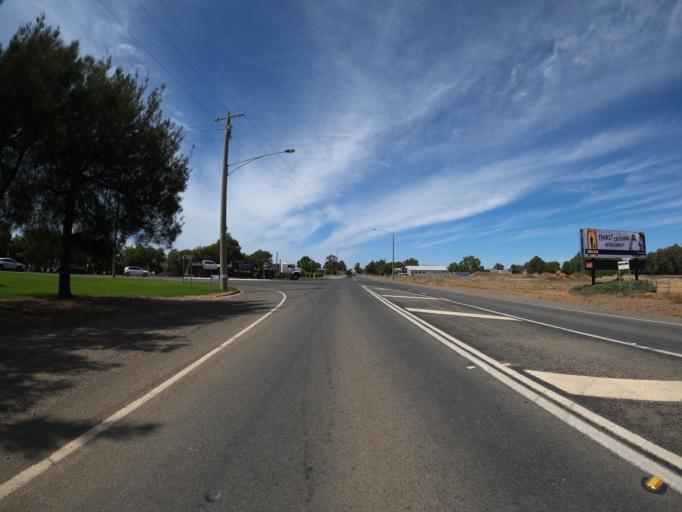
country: AU
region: Victoria
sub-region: Moira
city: Yarrawonga
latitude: -36.0265
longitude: 145.9956
